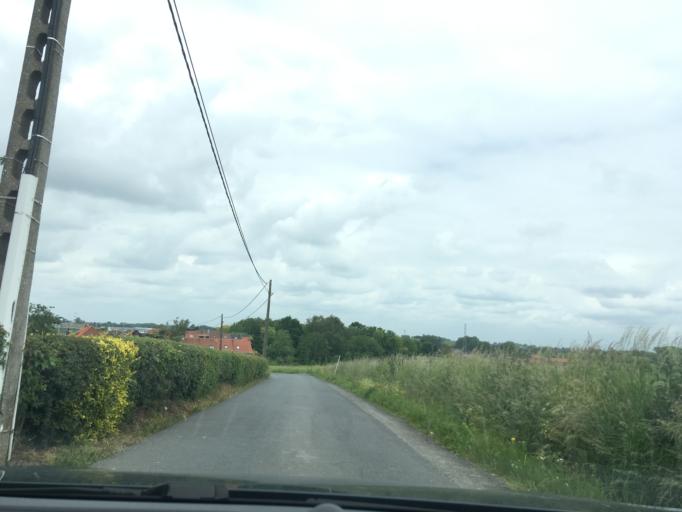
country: BE
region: Wallonia
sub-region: Province du Hainaut
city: Mouscron
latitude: 50.7614
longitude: 3.2059
